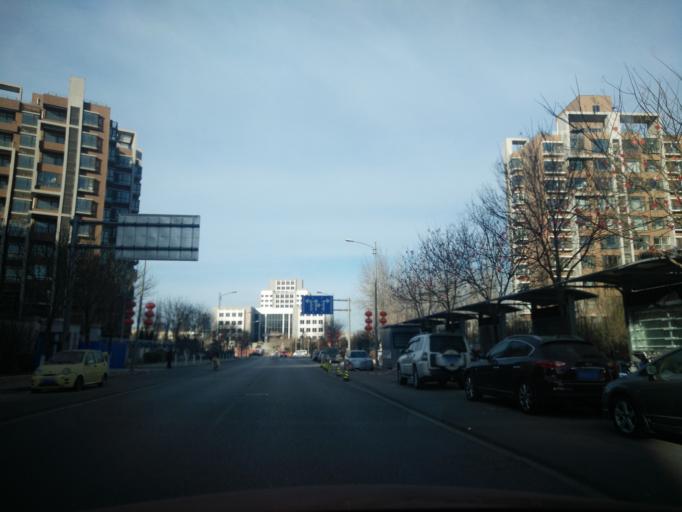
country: CN
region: Beijing
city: Jiugong
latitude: 39.7663
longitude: 116.4994
